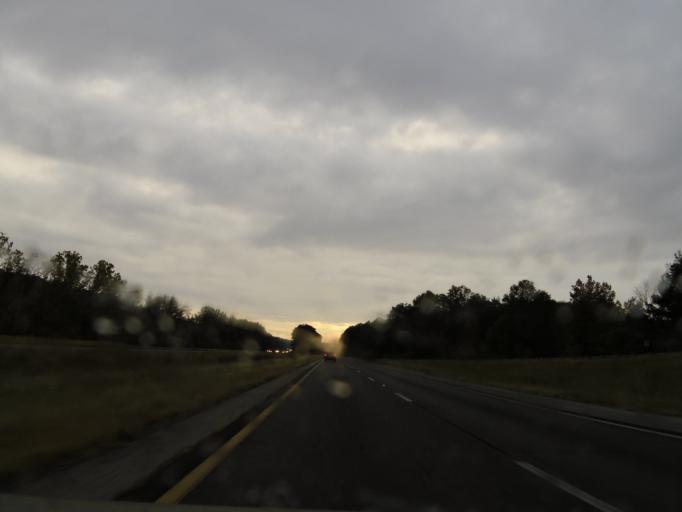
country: US
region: Alabama
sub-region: Saint Clair County
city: Springville
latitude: 33.7677
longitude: -86.4665
